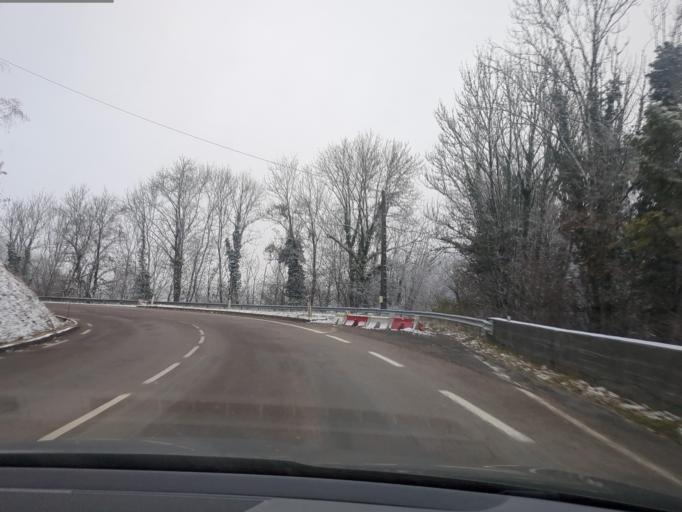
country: FR
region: Franche-Comte
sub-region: Departement du Jura
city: Perrigny
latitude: 46.6316
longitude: 5.6124
